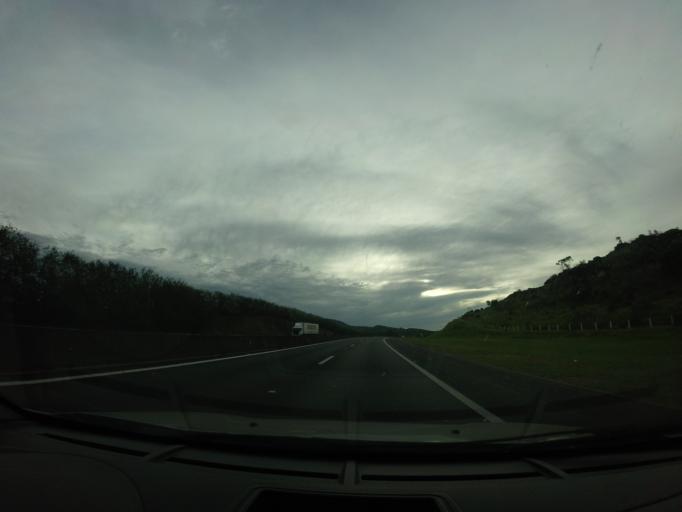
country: BR
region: Sao Paulo
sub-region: Valinhos
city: Valinhos
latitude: -22.9284
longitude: -46.9114
